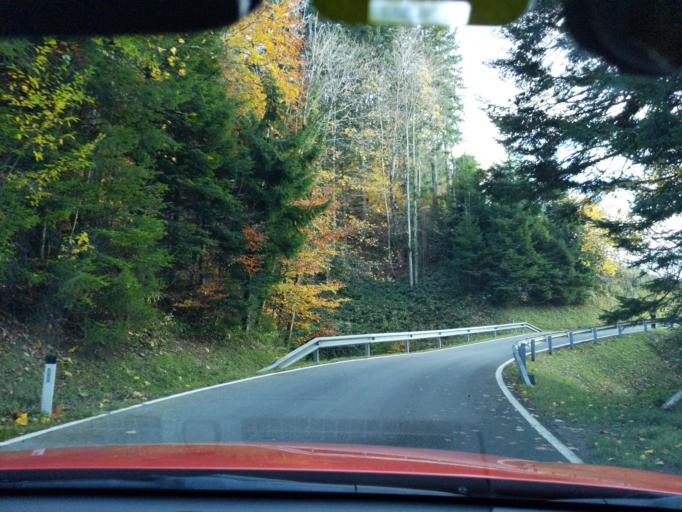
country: AT
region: Vorarlberg
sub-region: Politischer Bezirk Bregenz
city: Eichenberg
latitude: 47.5515
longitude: 9.7866
